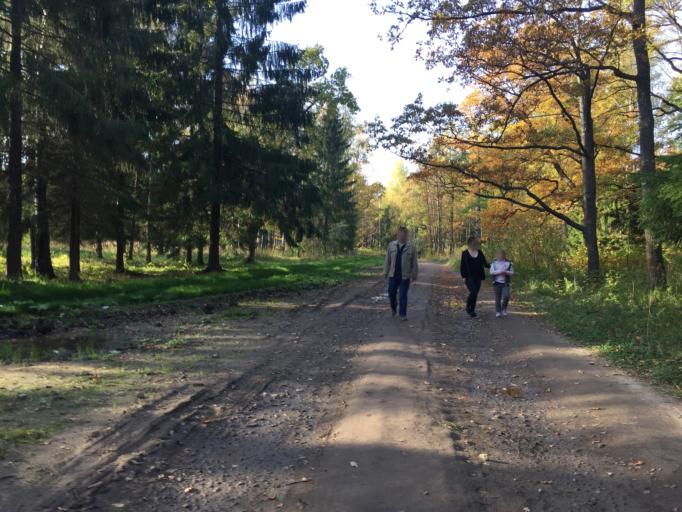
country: RU
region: St.-Petersburg
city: Pushkin
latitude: 59.7164
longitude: 30.3776
